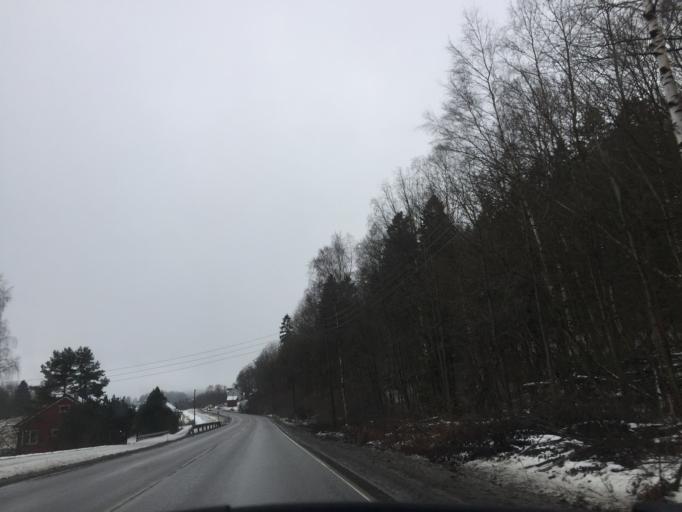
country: NO
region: Akershus
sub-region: Frogn
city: Drobak
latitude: 59.6834
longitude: 10.6672
